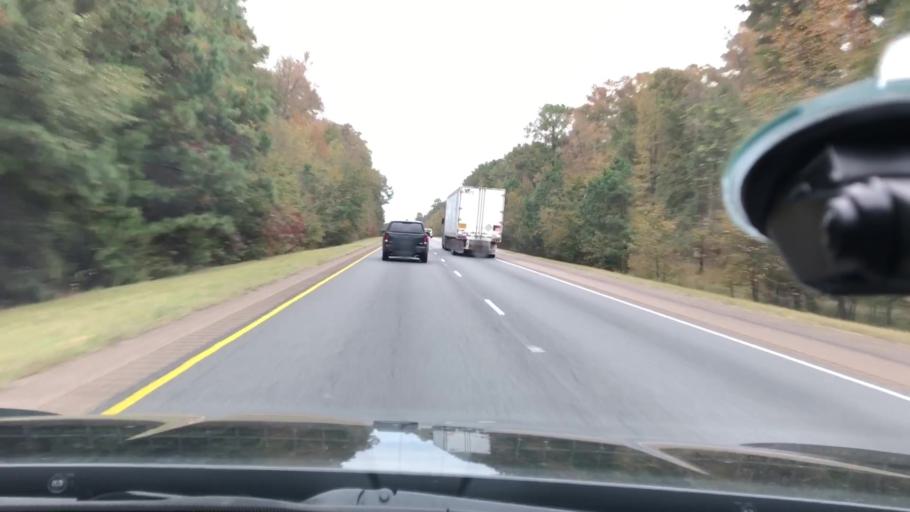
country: US
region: Arkansas
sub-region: Clark County
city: Gurdon
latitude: 33.9200
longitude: -93.2740
